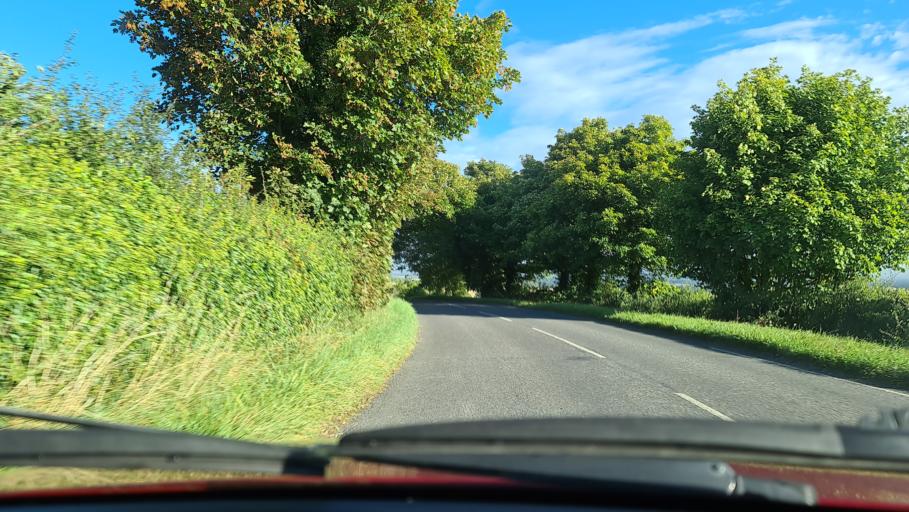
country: GB
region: England
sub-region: Buckinghamshire
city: Princes Risborough
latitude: 51.7000
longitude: -0.8645
